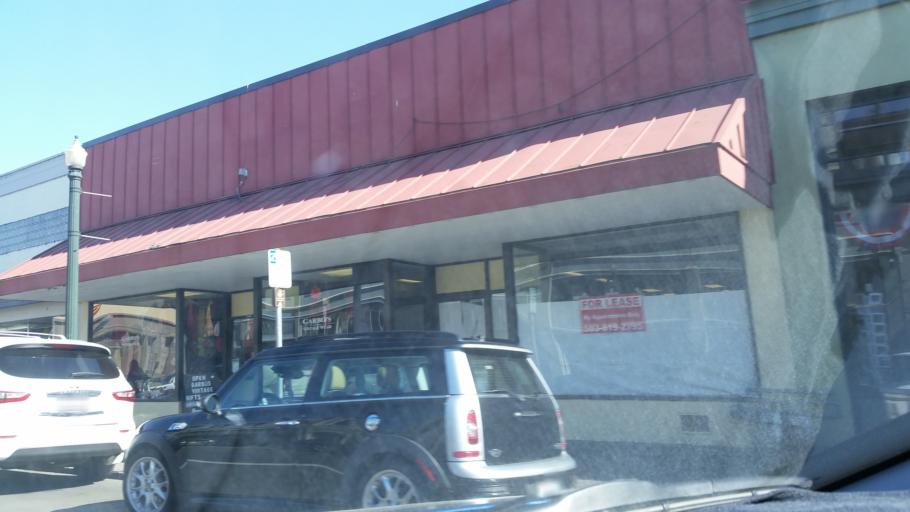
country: US
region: Oregon
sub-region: Clatsop County
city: Astoria
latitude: 46.1890
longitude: -123.8309
